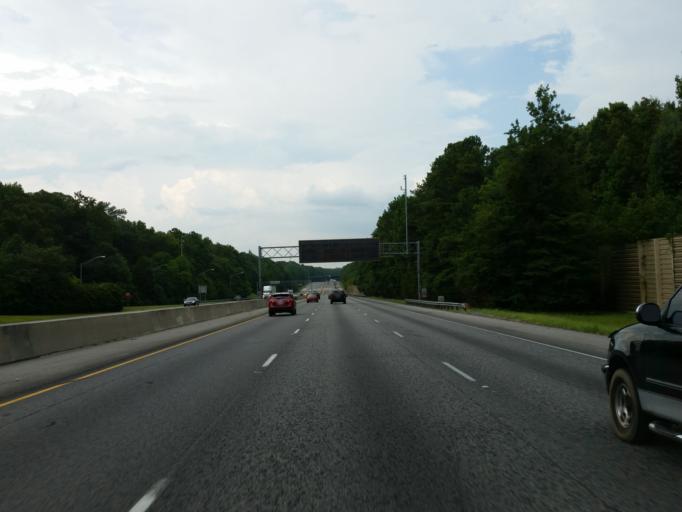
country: US
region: Georgia
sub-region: Bibb County
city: West Point
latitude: 32.8661
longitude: -83.7544
